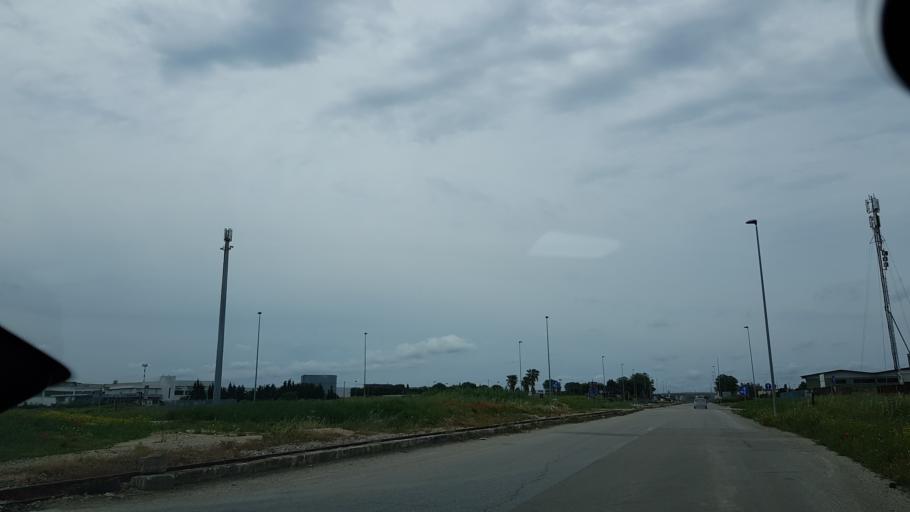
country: IT
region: Apulia
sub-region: Provincia di Brindisi
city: Materdomini
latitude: 40.6380
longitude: 17.9765
